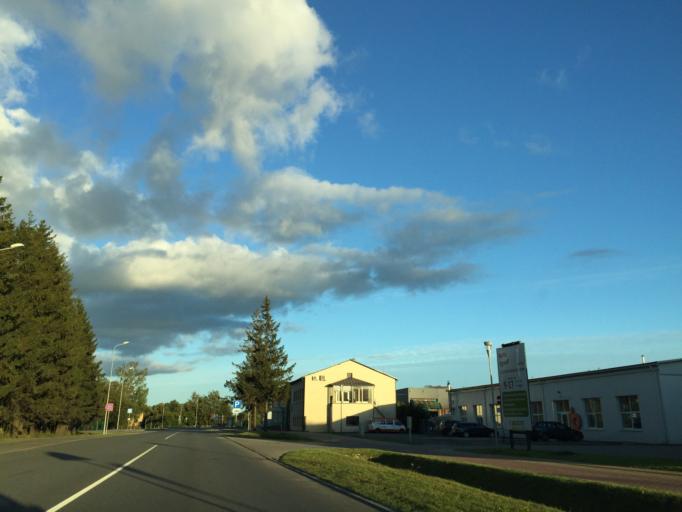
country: LV
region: Saldus Rajons
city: Saldus
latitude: 56.6853
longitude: 22.4668
